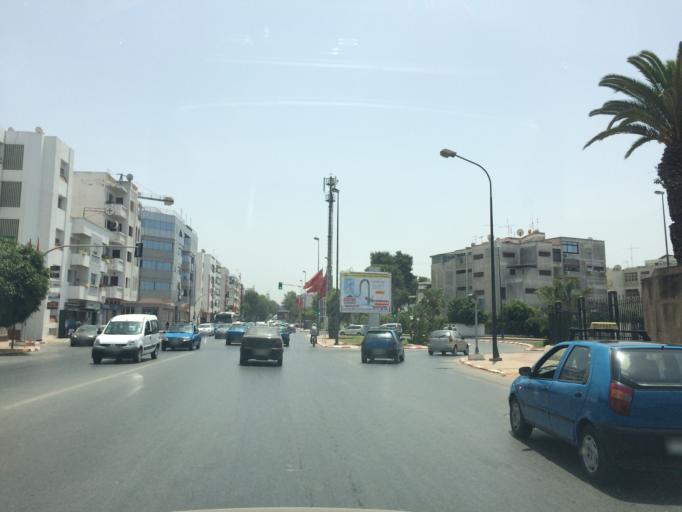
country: MA
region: Rabat-Sale-Zemmour-Zaer
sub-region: Rabat
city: Rabat
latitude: 34.0043
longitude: -6.8521
